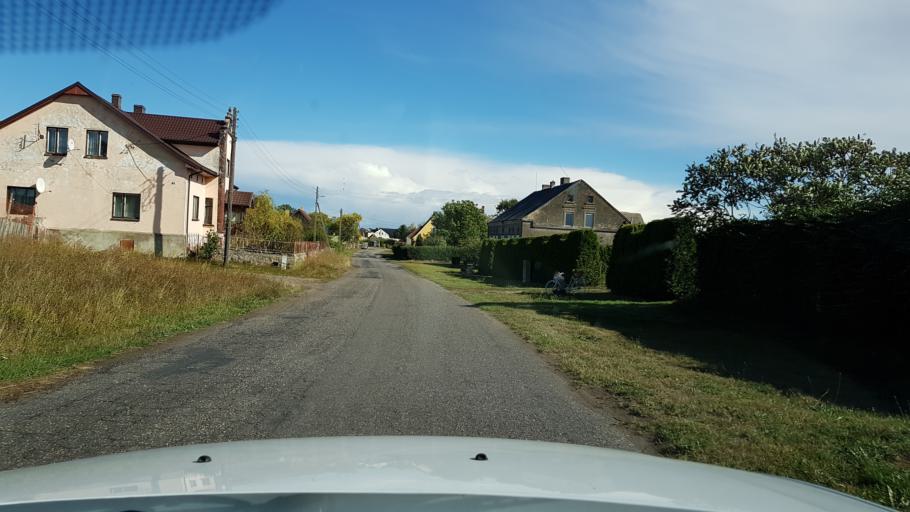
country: PL
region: West Pomeranian Voivodeship
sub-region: Powiat gryfinski
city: Banie
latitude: 53.1425
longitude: 14.6449
